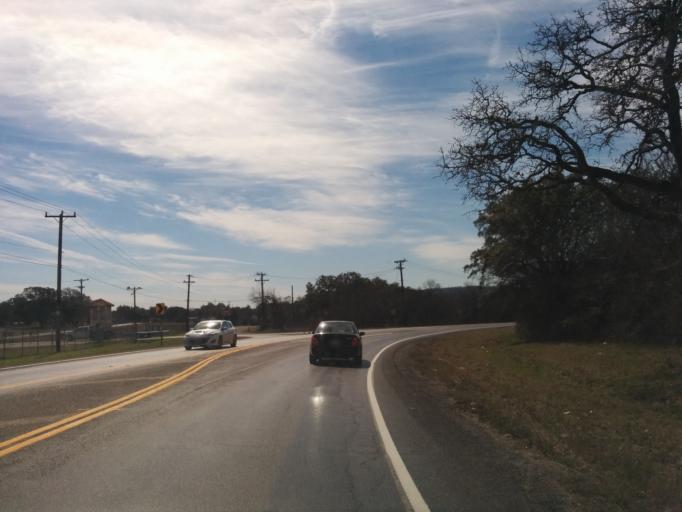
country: US
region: Texas
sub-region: Bexar County
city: Cross Mountain
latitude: 29.6799
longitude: -98.6315
